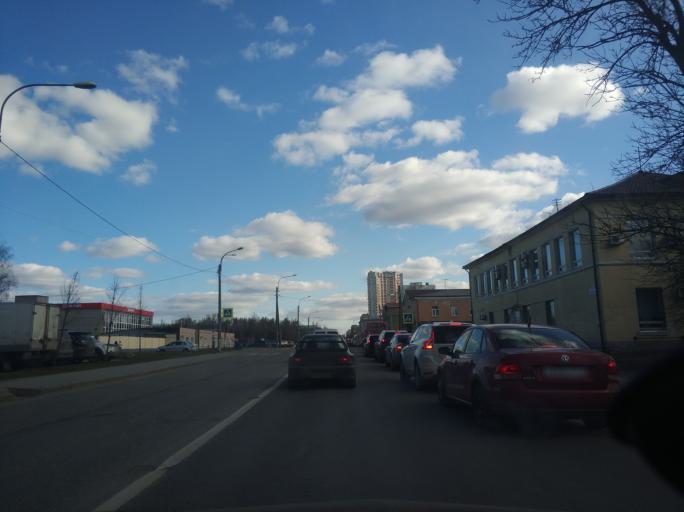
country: RU
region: St.-Petersburg
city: Krasnogvargeisky
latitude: 59.9641
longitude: 30.4864
